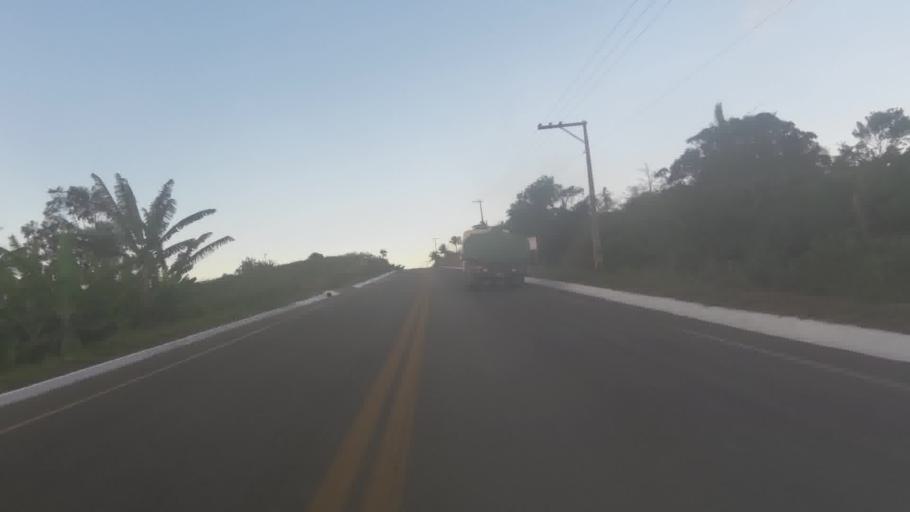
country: BR
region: Espirito Santo
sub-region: Marataizes
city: Marataizes
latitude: -21.1326
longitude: -40.8680
